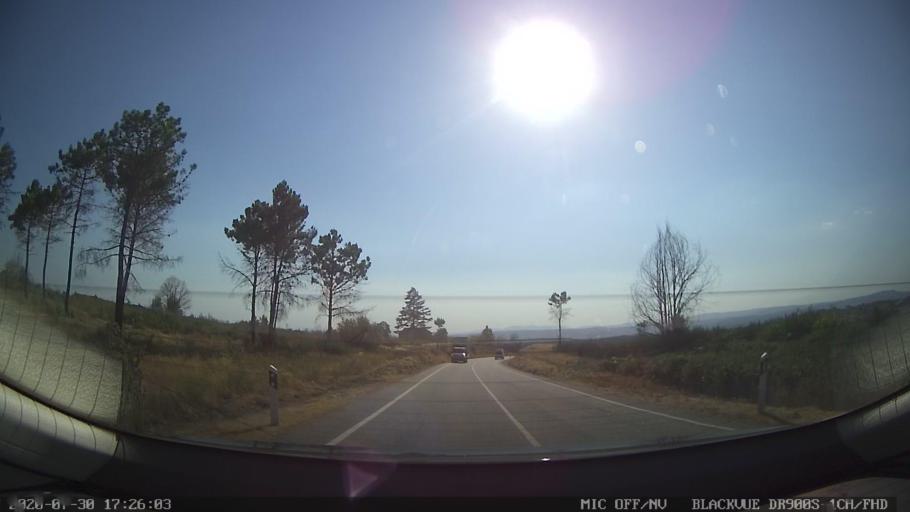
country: PT
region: Vila Real
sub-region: Murca
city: Murca
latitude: 41.3155
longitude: -7.4696
